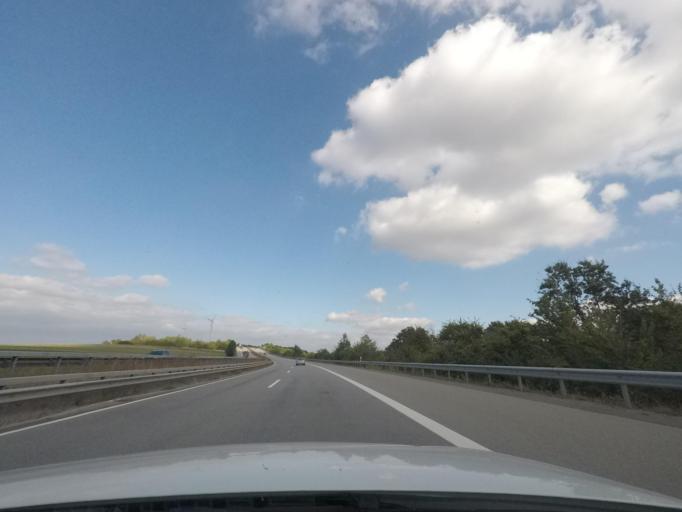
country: DE
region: Rheinland-Pfalz
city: Tiefenthal
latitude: 49.5348
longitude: 8.1098
